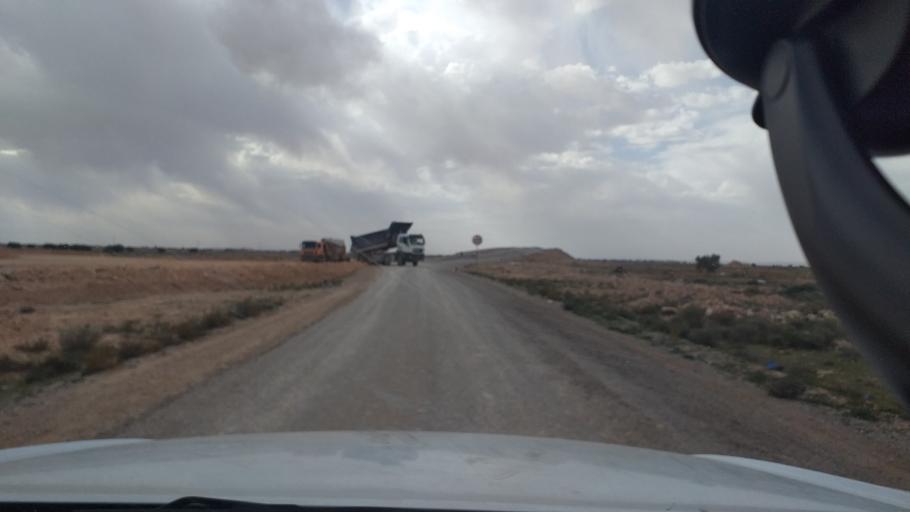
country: TN
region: Madanin
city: Medenine
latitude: 33.3035
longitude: 10.6111
